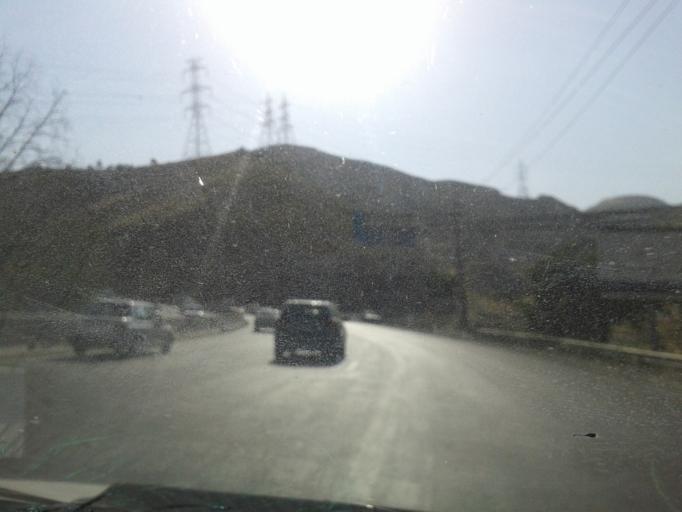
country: IR
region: Tehran
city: Pakdasht
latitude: 35.7417
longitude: 51.6935
